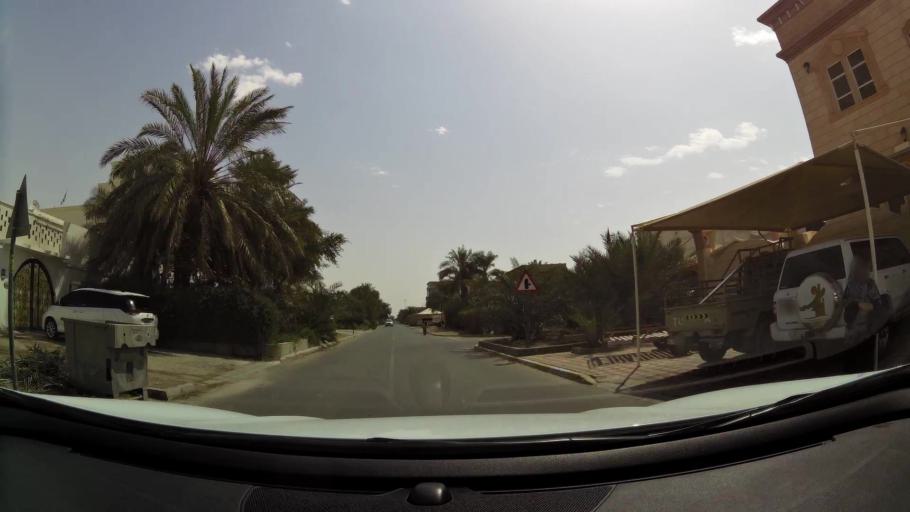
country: AE
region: Abu Dhabi
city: Abu Dhabi
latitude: 24.2935
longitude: 54.6350
